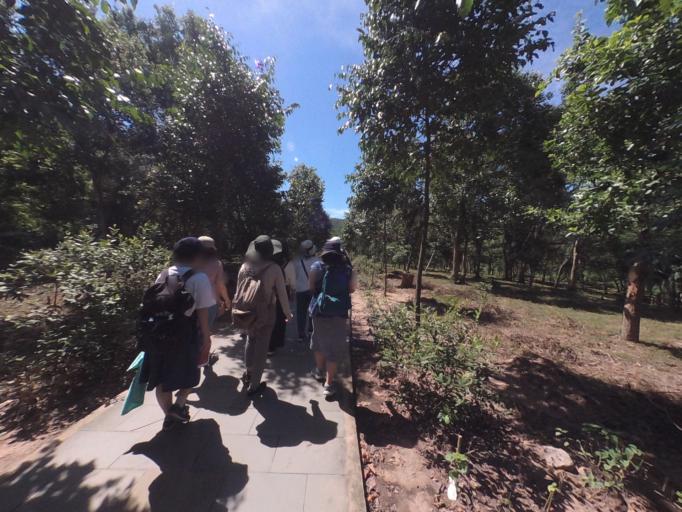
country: VN
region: Quang Nam
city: Dai Loc
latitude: 15.7671
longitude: 108.1216
